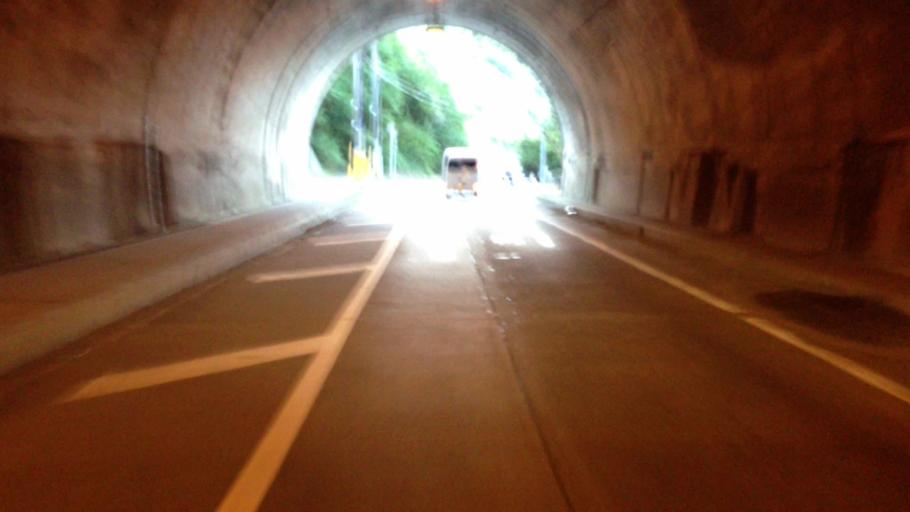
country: JP
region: Kanagawa
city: Yokosuka
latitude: 35.2346
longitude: 139.6581
